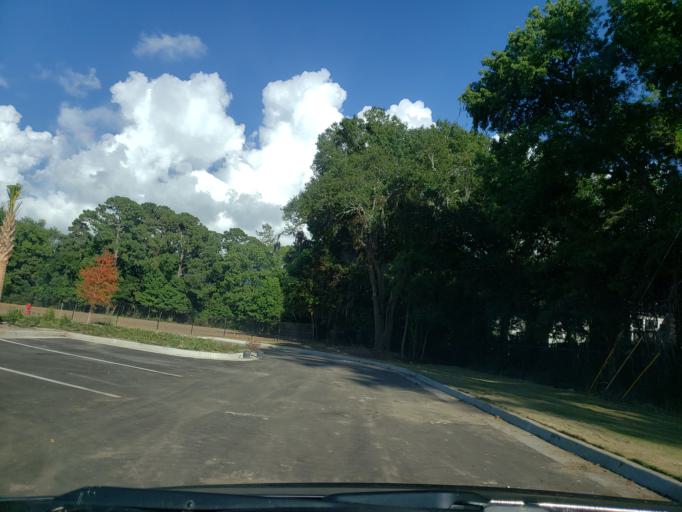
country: US
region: Georgia
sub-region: Chatham County
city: Montgomery
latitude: 31.9902
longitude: -81.1268
